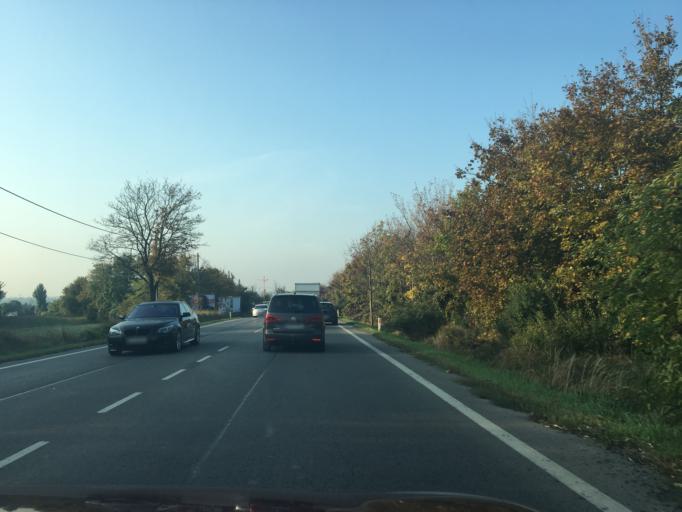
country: AT
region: Lower Austria
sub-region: Politischer Bezirk Korneuburg
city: Hagenbrunn
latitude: 48.3064
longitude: 16.4257
